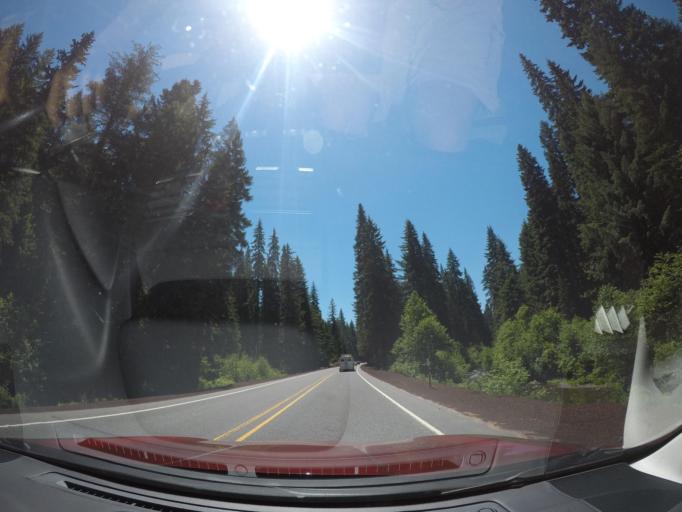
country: US
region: Oregon
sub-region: Deschutes County
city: Sisters
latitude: 44.5405
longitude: -121.9956
